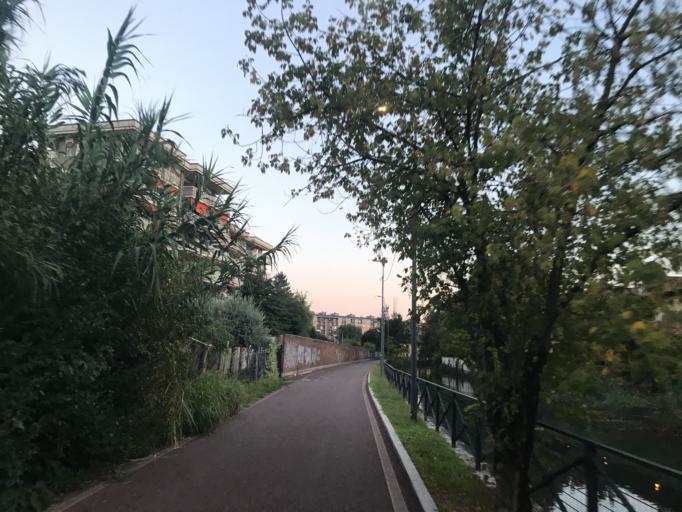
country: IT
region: Lombardy
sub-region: Citta metropolitana di Milano
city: Sesto San Giovanni
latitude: 45.5132
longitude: 9.2540
